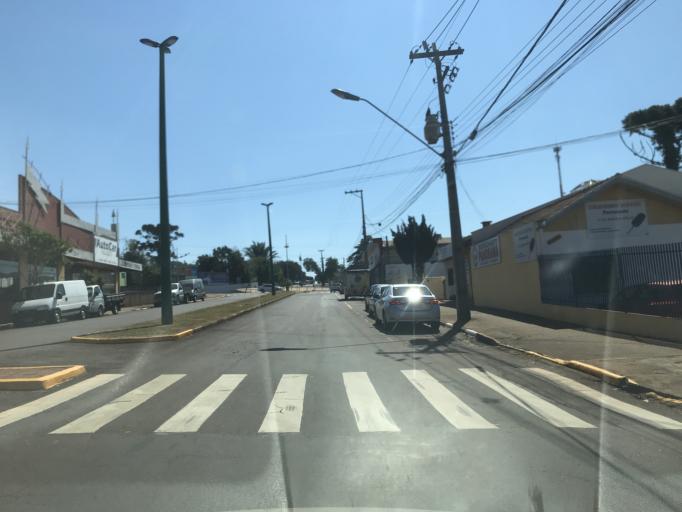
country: BR
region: Parana
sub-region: Toledo
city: Toledo
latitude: -24.7282
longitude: -53.7360
